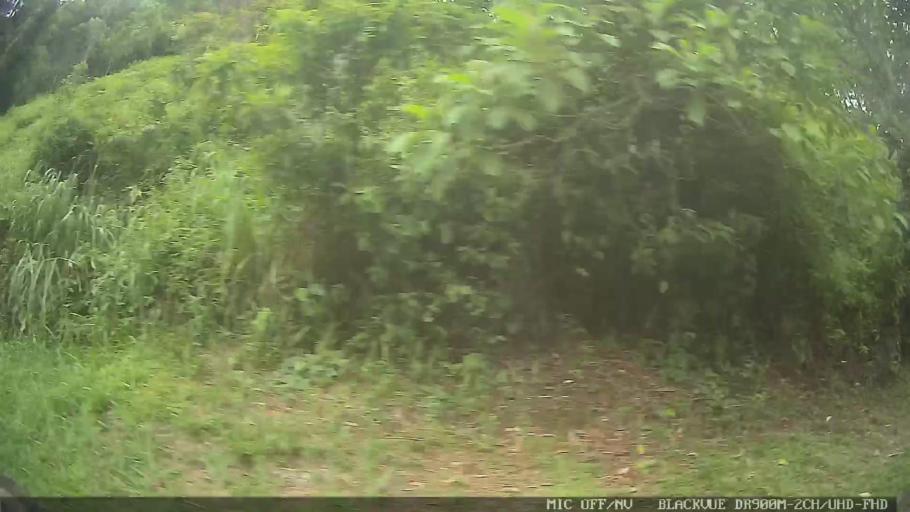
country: BR
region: Sao Paulo
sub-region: Caraguatatuba
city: Caraguatatuba
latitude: -23.6016
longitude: -45.4397
